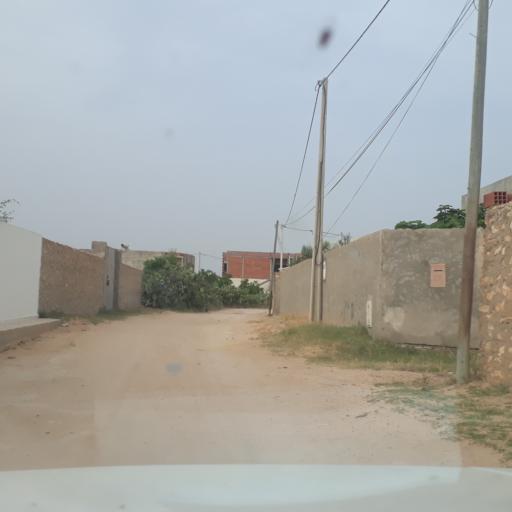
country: TN
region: Safaqis
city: Al Qarmadah
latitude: 34.8270
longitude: 10.7760
